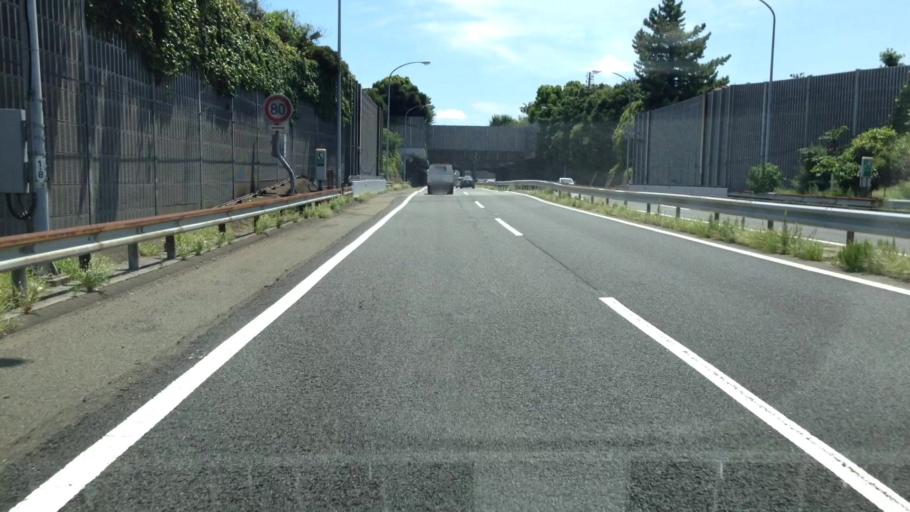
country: JP
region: Kanagawa
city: Yokohama
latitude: 35.4060
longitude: 139.5752
